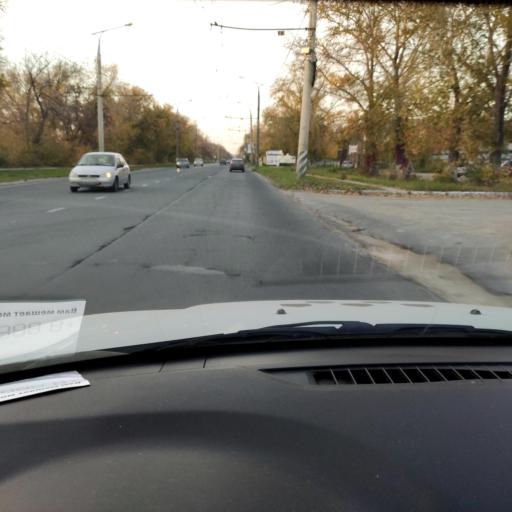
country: RU
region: Samara
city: Tol'yatti
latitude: 53.5305
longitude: 49.4378
